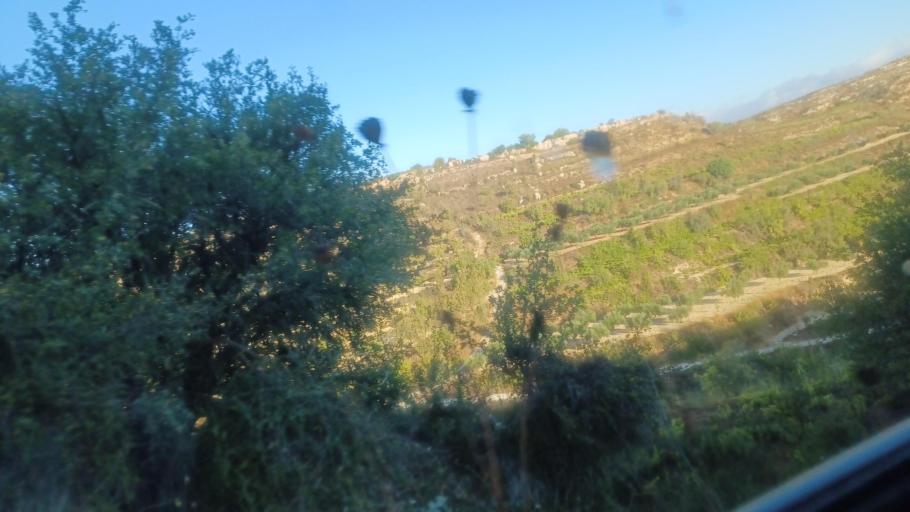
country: CY
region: Pafos
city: Mesogi
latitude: 34.8511
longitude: 32.4687
